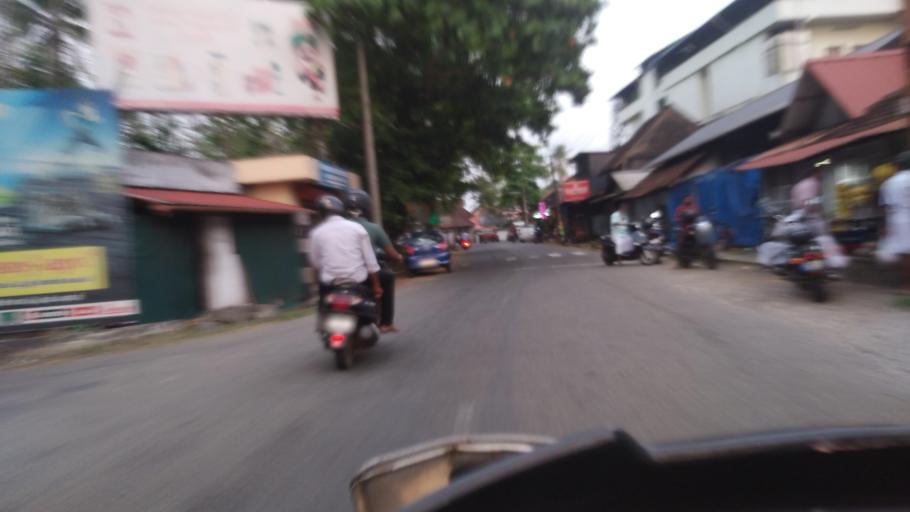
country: IN
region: Kerala
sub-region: Thrissur District
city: Kodungallur
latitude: 10.1514
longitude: 76.2226
